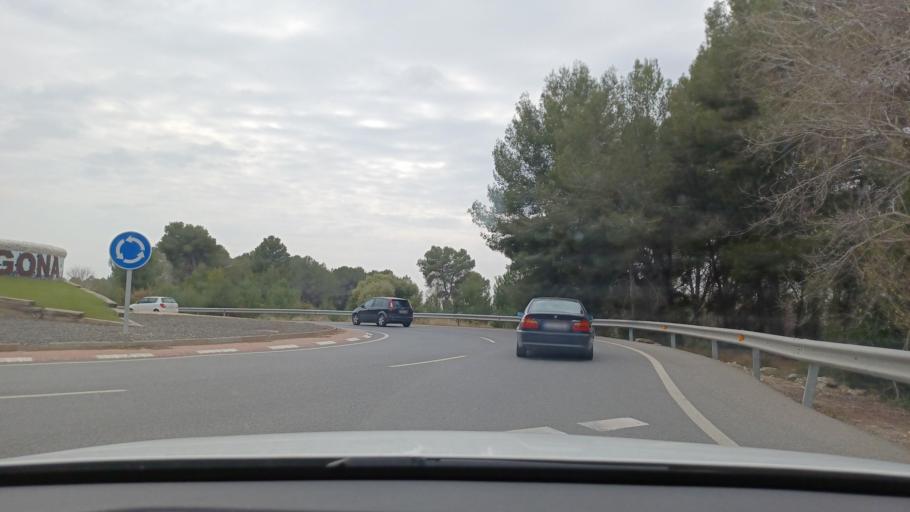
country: ES
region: Catalonia
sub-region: Provincia de Tarragona
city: els Pallaresos
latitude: 41.1634
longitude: 1.2397
